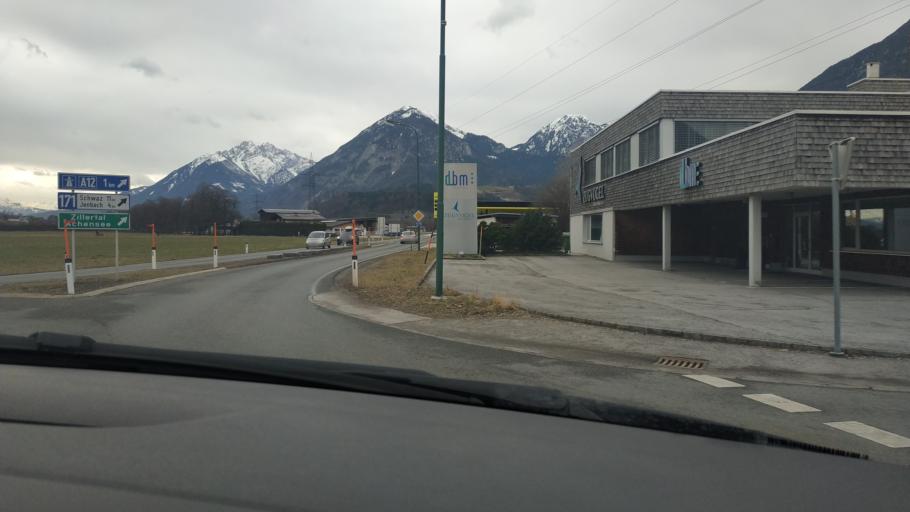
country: AT
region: Tyrol
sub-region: Politischer Bezirk Schwaz
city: Strass im Zillertal
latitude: 47.3978
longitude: 11.8175
